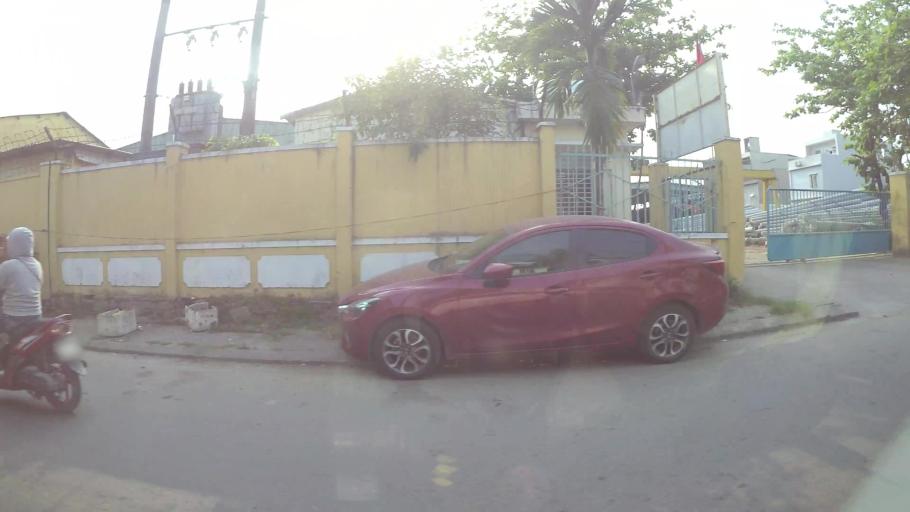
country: VN
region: Da Nang
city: Lien Chieu
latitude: 16.0543
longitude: 108.1668
